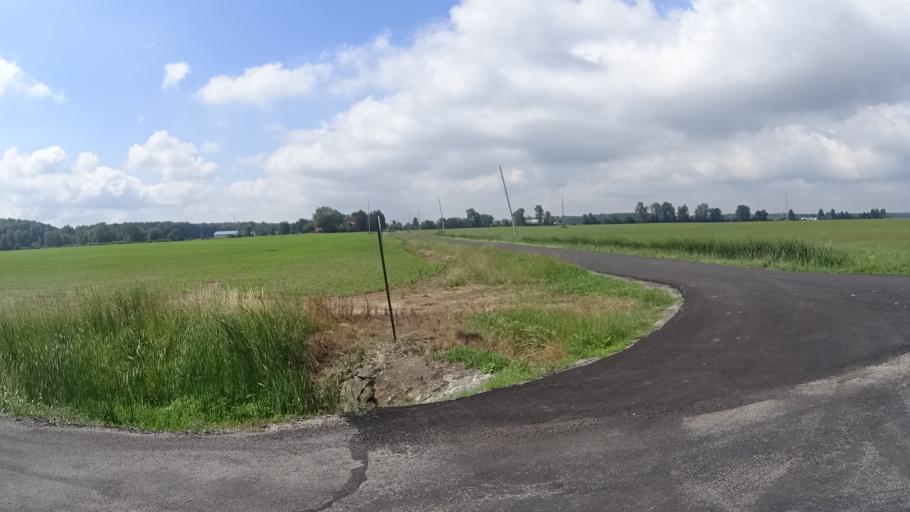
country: US
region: Ohio
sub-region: Huron County
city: Wakeman
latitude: 41.2839
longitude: -82.4425
